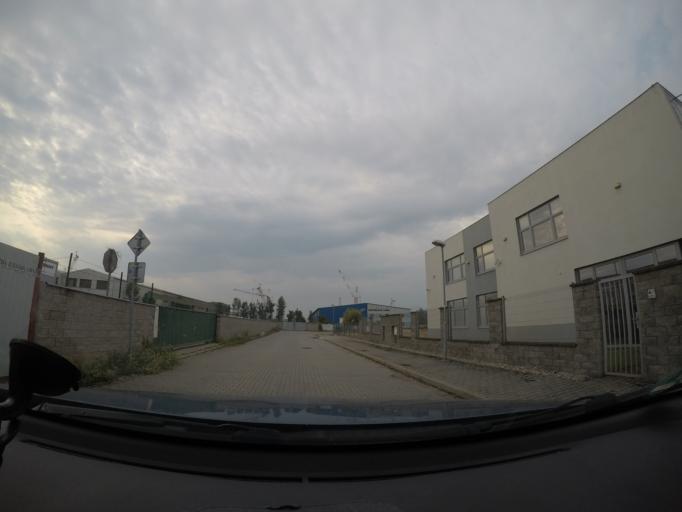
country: SK
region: Trenciansky
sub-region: Okres Trencin
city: Trencin
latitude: 48.8887
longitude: 18.0101
